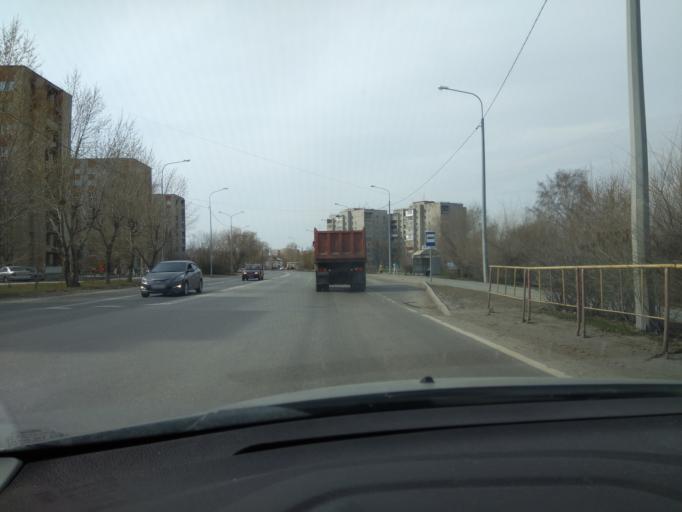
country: RU
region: Tjumen
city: Melioratorov
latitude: 57.1853
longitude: 65.5842
